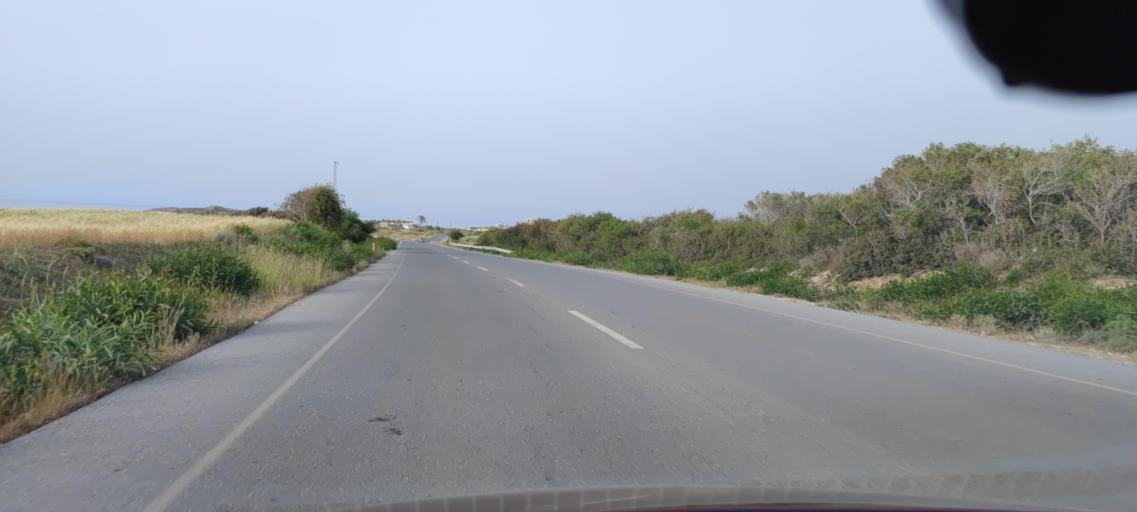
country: CY
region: Ammochostos
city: Rizokarpaso
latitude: 35.5641
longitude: 34.2469
